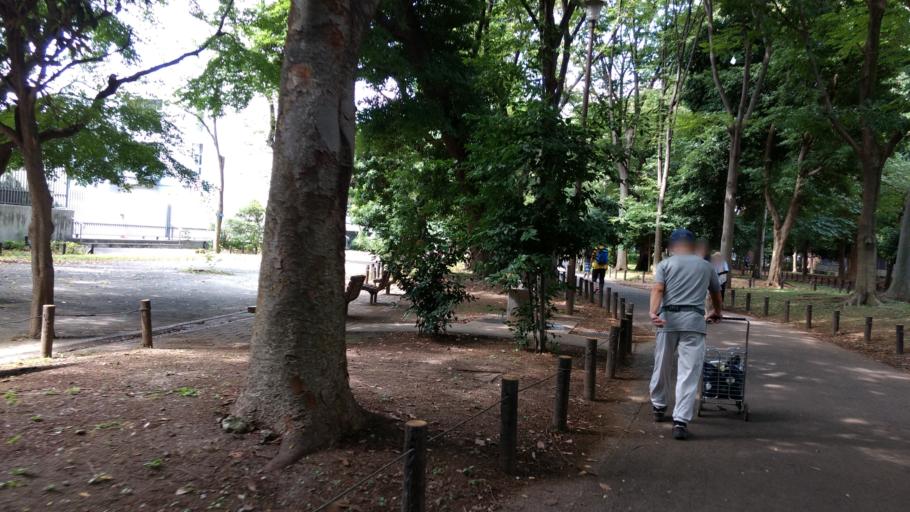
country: JP
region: Tokyo
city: Tokyo
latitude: 35.7069
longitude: 139.7072
